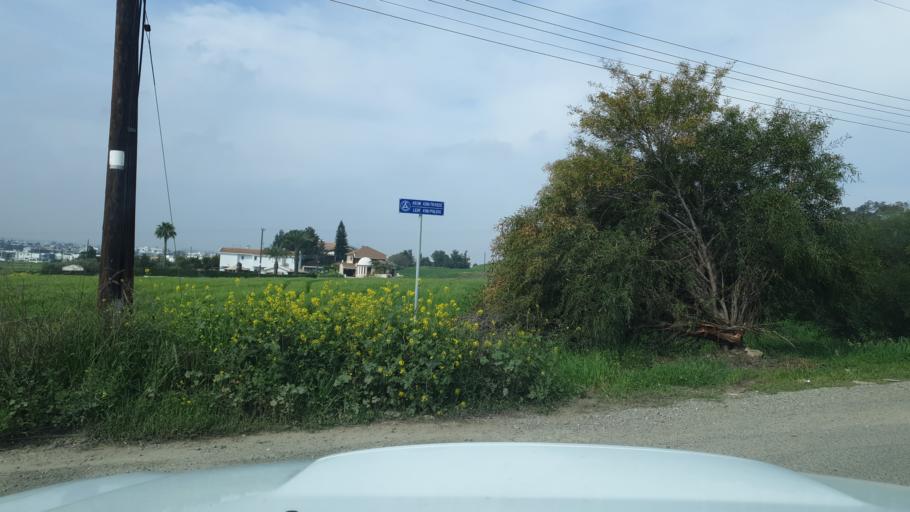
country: CY
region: Lefkosia
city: Tseri
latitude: 35.1190
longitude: 33.3448
